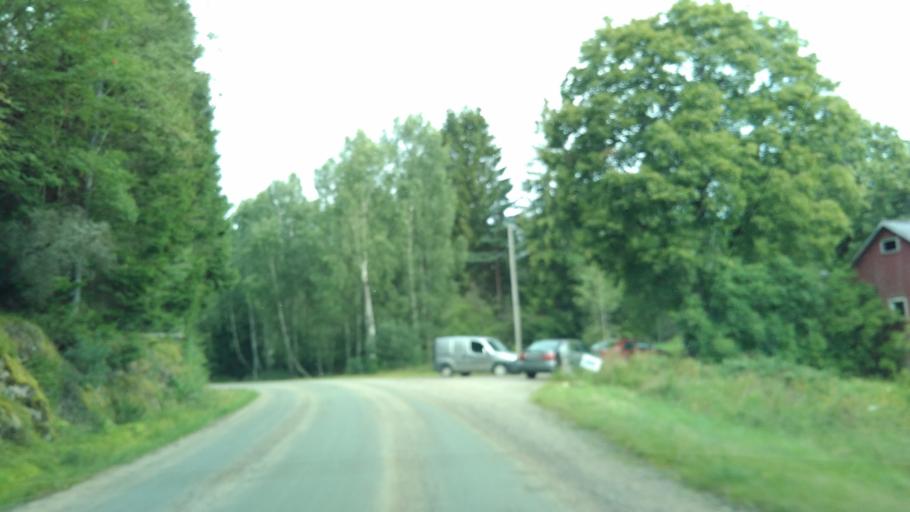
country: SE
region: Vaestra Goetaland
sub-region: Marks Kommun
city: Fritsla
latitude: 57.5745
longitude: 12.7698
